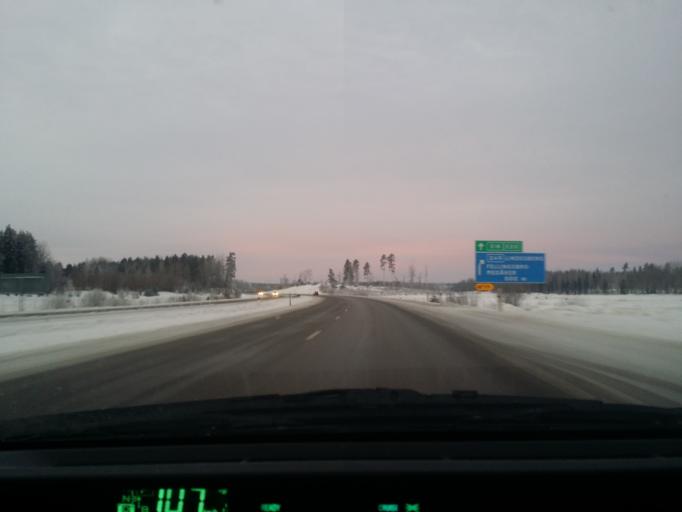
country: SE
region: Vaestmanland
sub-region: Arboga Kommun
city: Arboga
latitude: 59.4206
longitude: 15.7797
